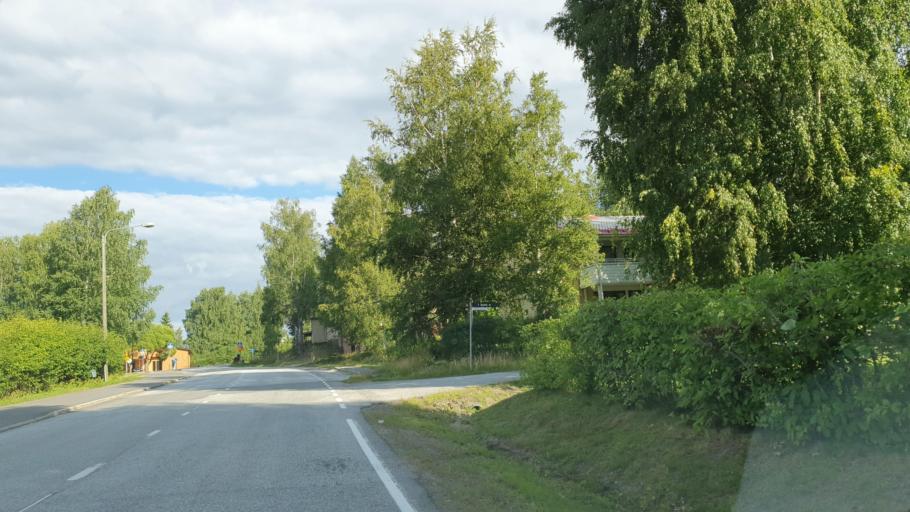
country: FI
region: Central Finland
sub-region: Jyvaeskylae
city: Saeynaetsalo
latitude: 62.1556
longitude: 25.7567
